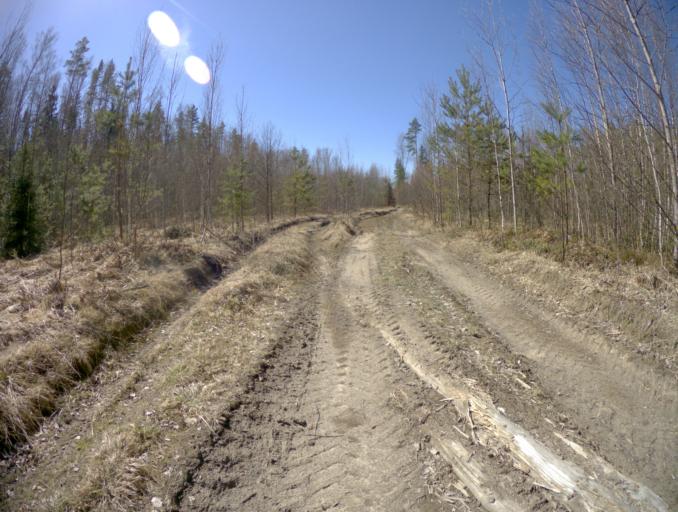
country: RU
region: Vladimir
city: Ivanishchi
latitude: 55.8368
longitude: 40.4530
